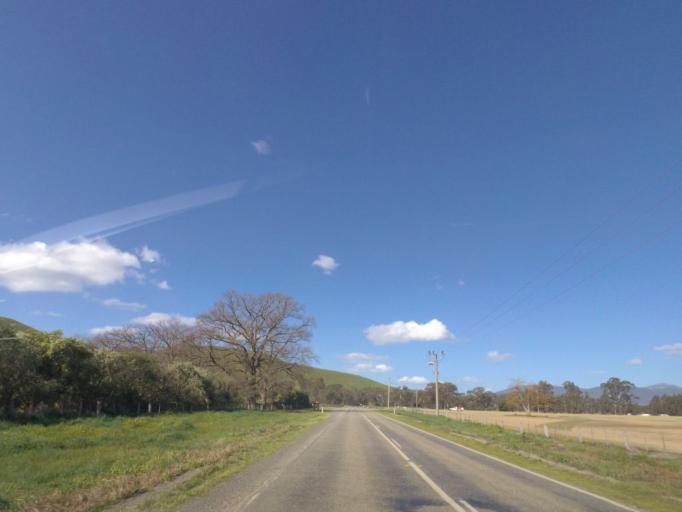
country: AU
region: Victoria
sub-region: Murrindindi
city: Alexandra
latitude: -37.2281
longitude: 145.7563
